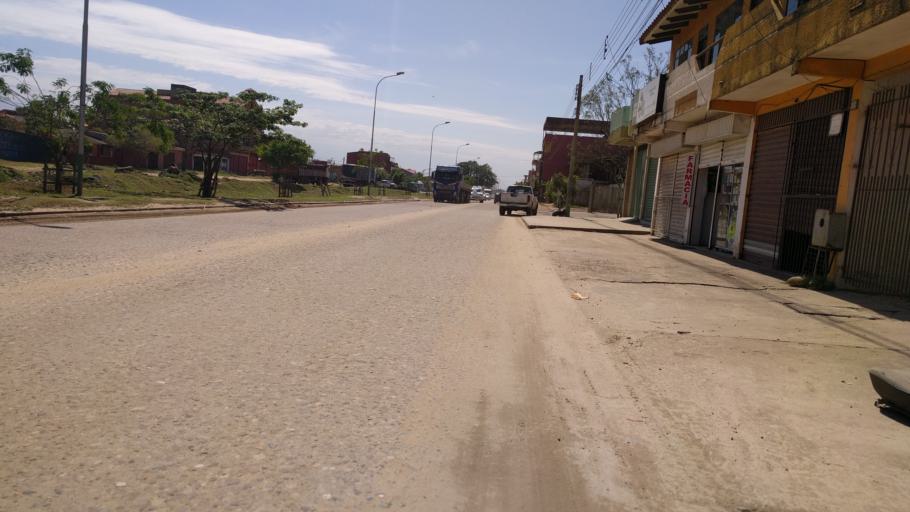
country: BO
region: Santa Cruz
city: Santa Cruz de la Sierra
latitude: -17.8212
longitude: -63.2297
